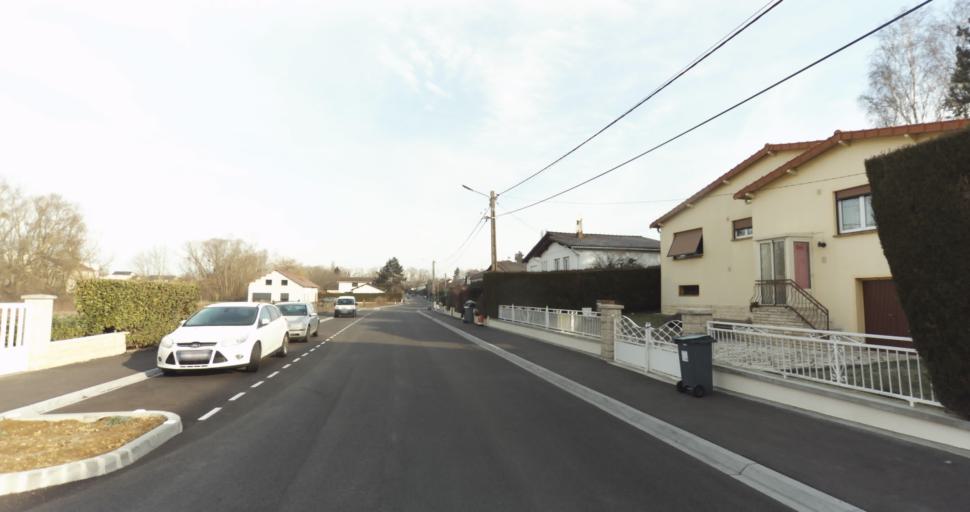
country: FR
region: Lorraine
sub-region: Departement de Meurthe-et-Moselle
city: Jarny
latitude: 49.1587
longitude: 5.8880
